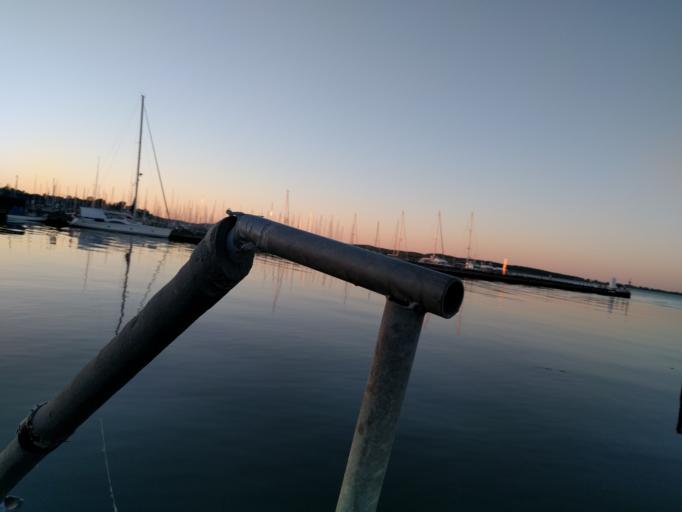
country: DK
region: South Denmark
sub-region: Kerteminde Kommune
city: Kerteminde
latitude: 55.4502
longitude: 10.6661
